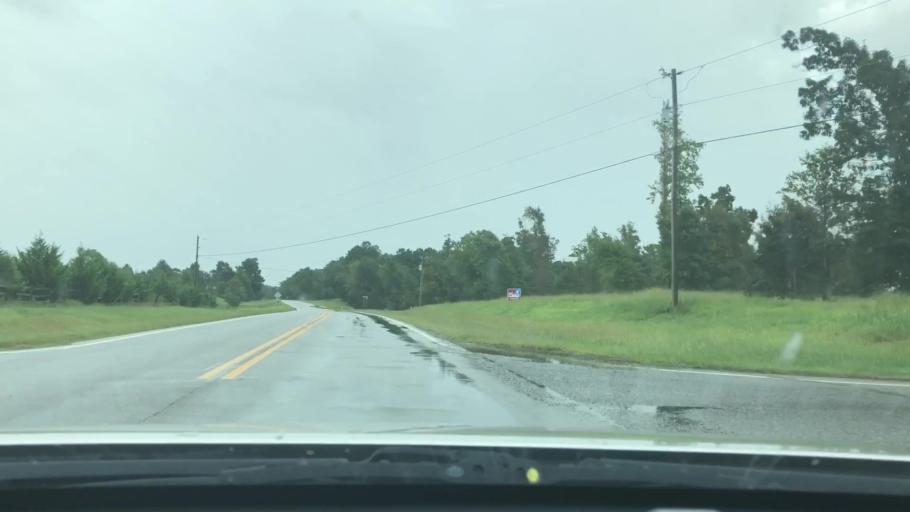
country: US
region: Georgia
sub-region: Lamar County
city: Barnesville
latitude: 33.0593
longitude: -84.2020
